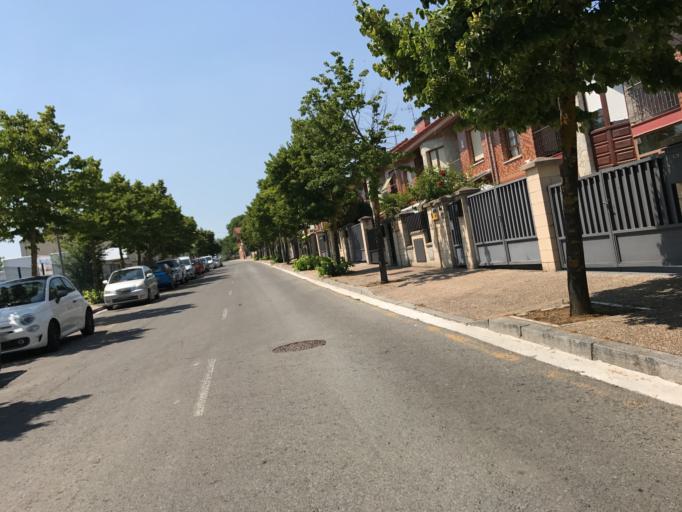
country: ES
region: Basque Country
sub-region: Provincia de Alava
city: Gasteiz / Vitoria
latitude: 42.8785
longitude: -2.6834
